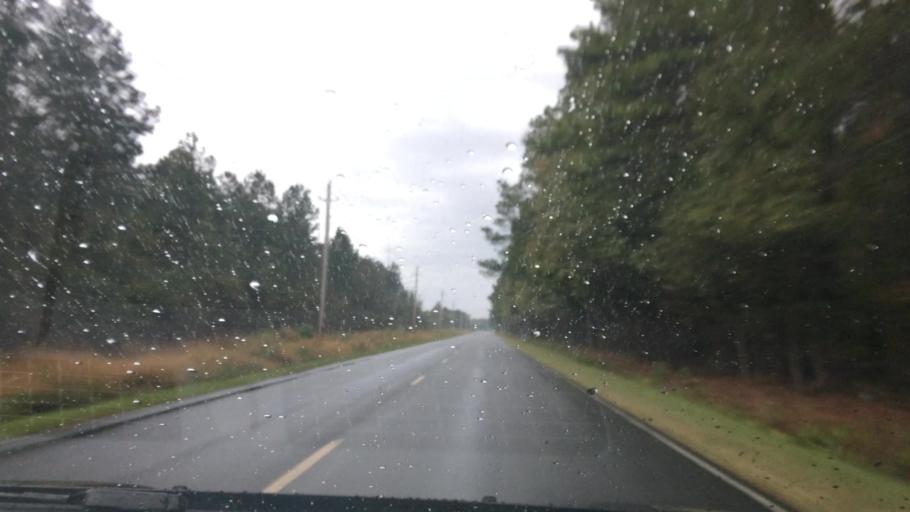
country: US
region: North Carolina
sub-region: Pitt County
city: Grifton
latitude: 35.3986
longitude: -77.4039
